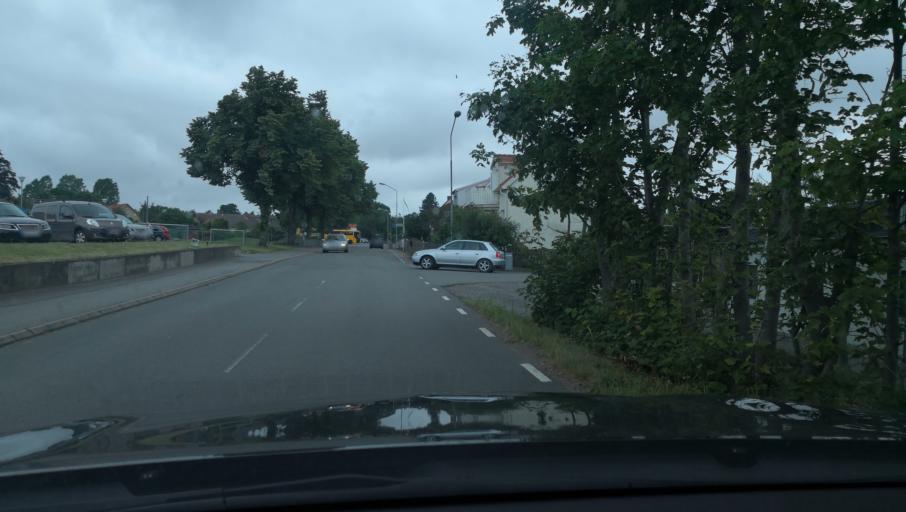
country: SE
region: Skane
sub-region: Simrishamns Kommun
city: Kivik
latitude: 55.6841
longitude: 14.2296
